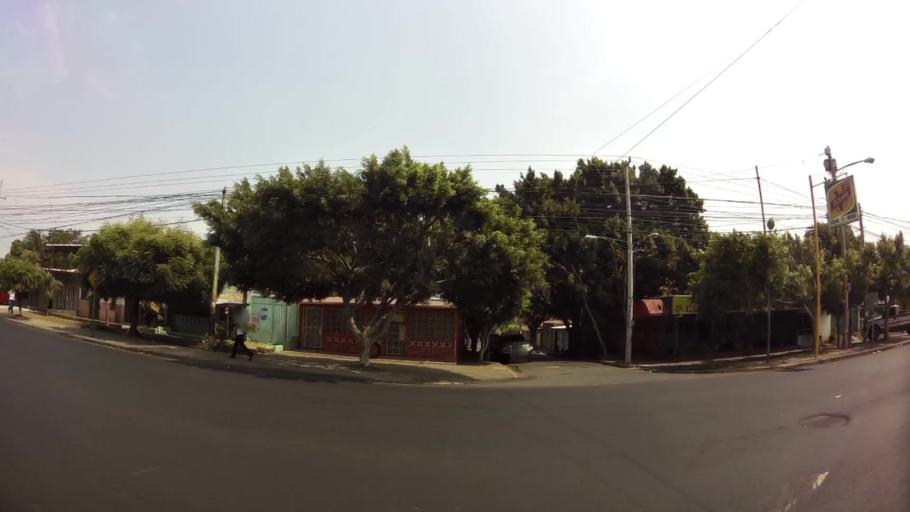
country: NI
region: Managua
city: Ciudad Sandino
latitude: 12.1383
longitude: -86.3034
